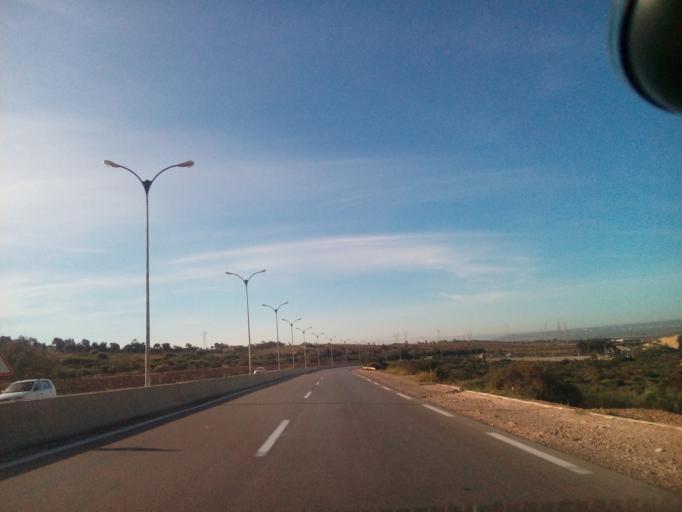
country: DZ
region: Oran
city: Ain el Bya
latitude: 35.7916
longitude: -0.0940
